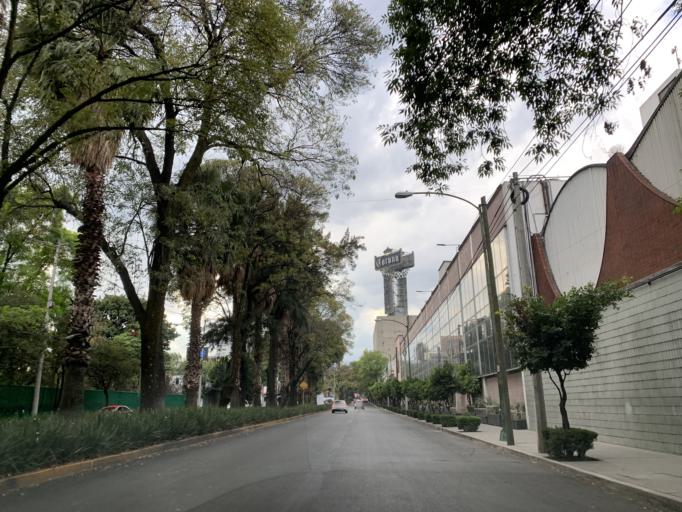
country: MX
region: Mexico City
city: Miguel Hidalgo
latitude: 19.4403
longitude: -99.1878
